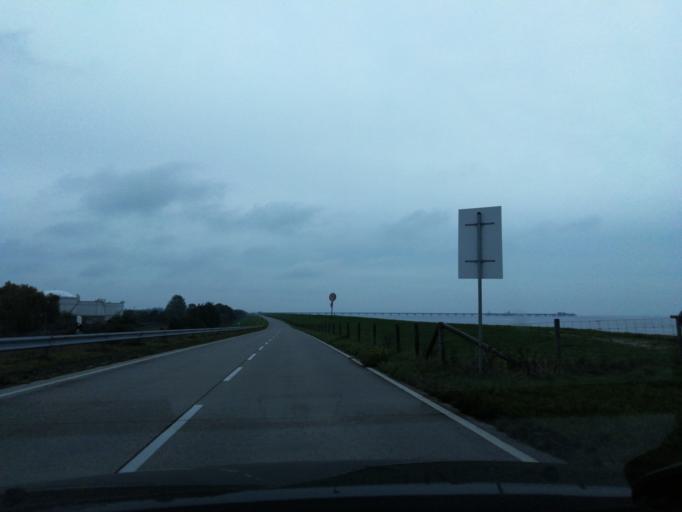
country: DE
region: Lower Saxony
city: Wilhelmshaven
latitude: 53.6161
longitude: 8.1114
